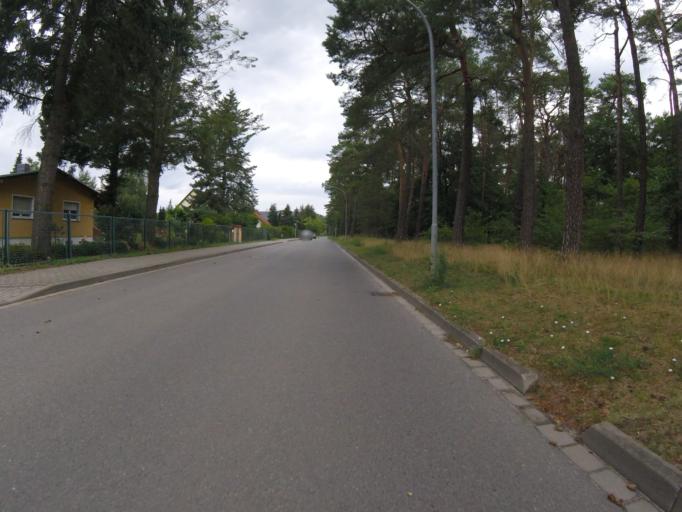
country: DE
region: Brandenburg
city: Konigs Wusterhausen
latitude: 52.2984
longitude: 13.6377
